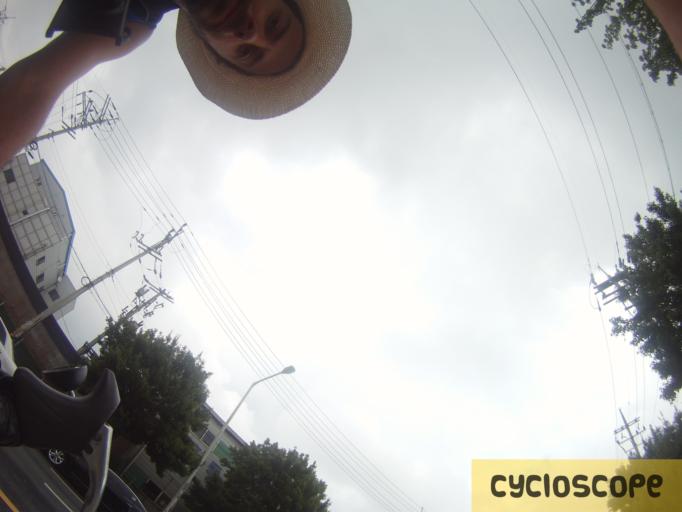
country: KR
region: Gyeonggi-do
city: Hwaseong-si
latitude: 37.0651
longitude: 126.7993
